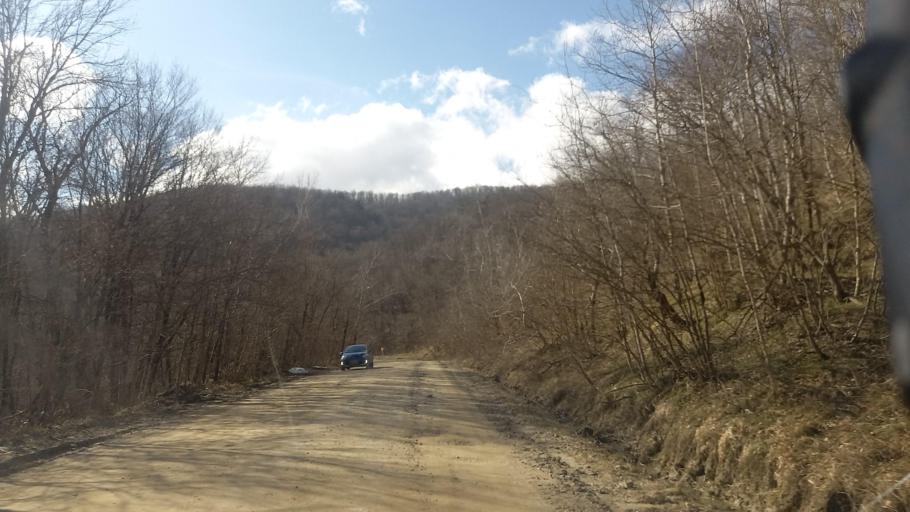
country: RU
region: Krasnodarskiy
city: Smolenskaya
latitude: 44.6496
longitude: 38.7279
